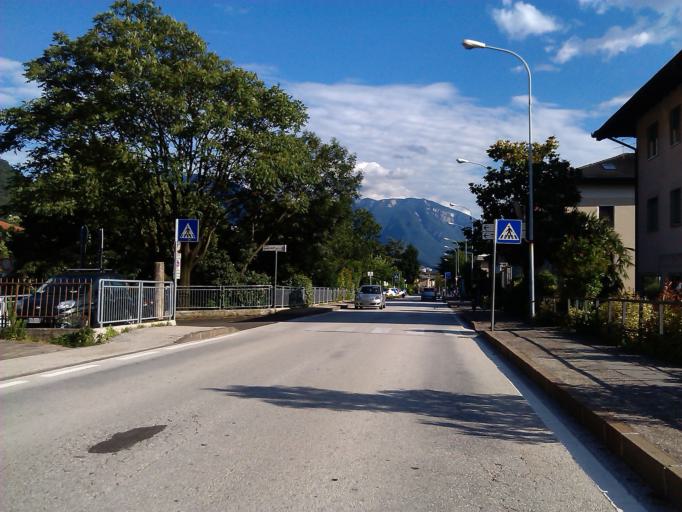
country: IT
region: Trentino-Alto Adige
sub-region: Provincia di Trento
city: Meano
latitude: 46.1078
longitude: 11.1117
